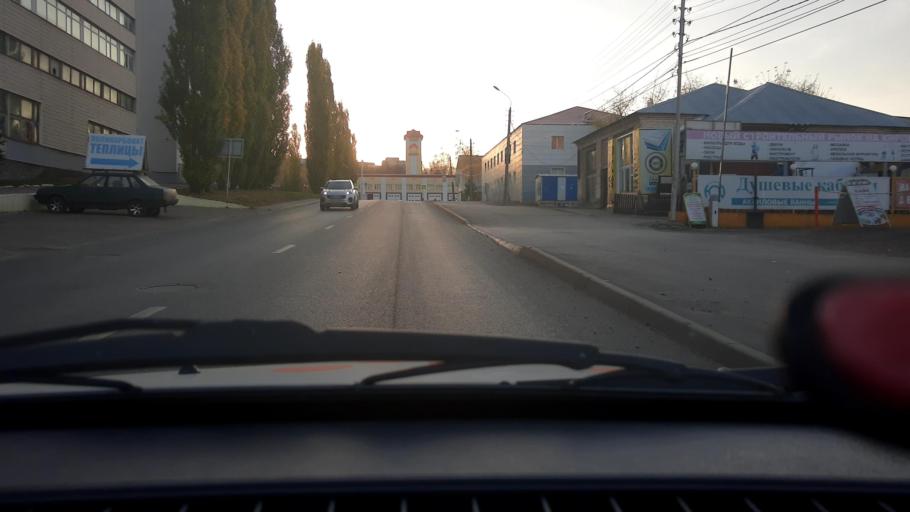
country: RU
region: Bashkortostan
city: Ufa
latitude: 54.7462
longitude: 55.9745
